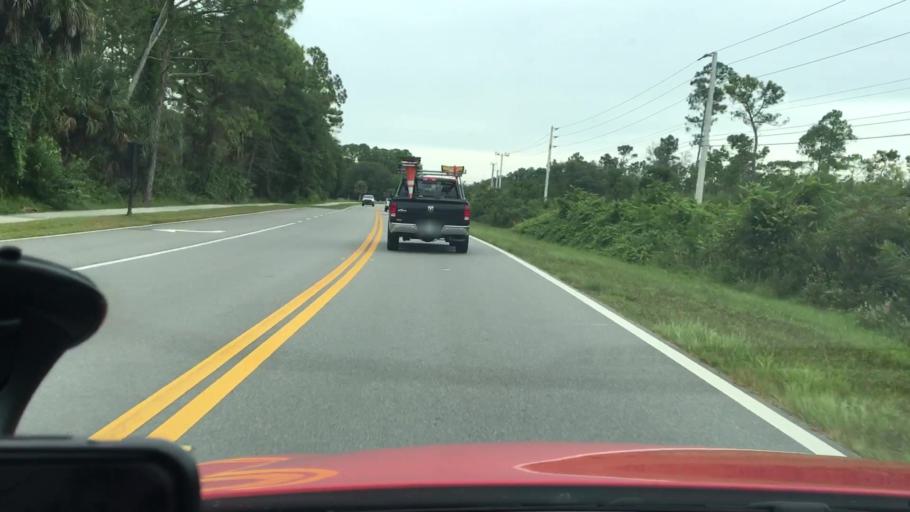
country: US
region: Florida
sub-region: Flagler County
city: Flagler Beach
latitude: 29.4999
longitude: -81.1906
